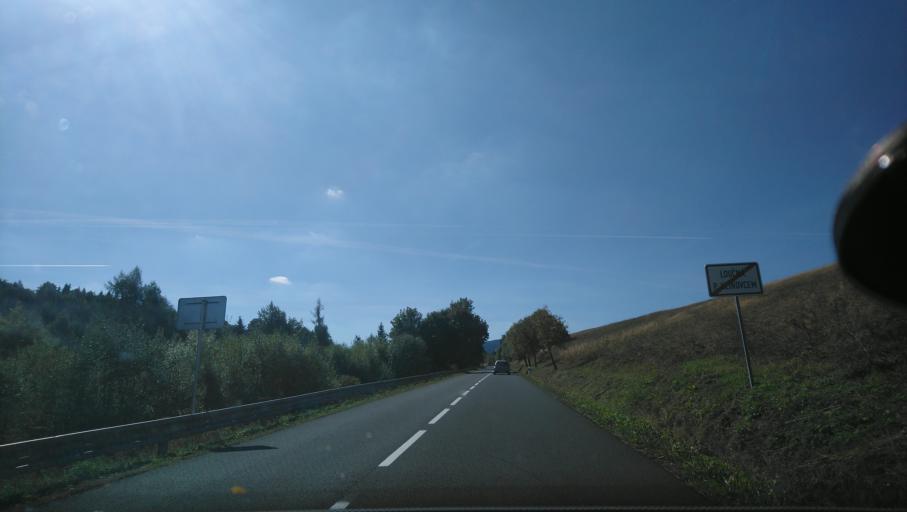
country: DE
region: Saxony
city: Kurort Oberwiesenthal
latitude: 50.4261
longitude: 13.0007
